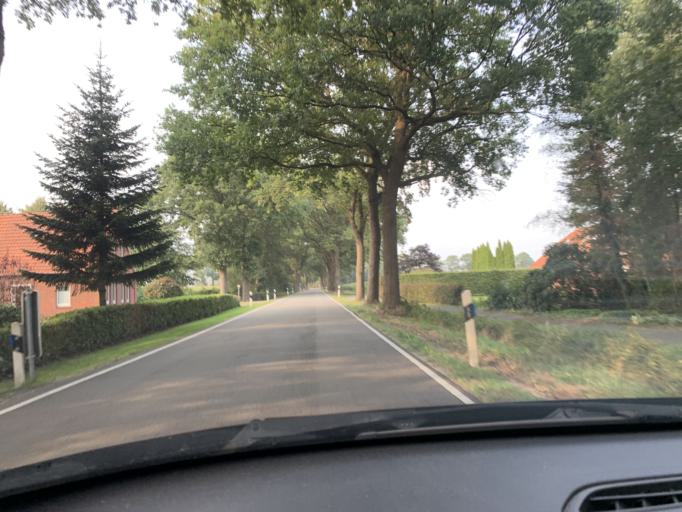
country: DE
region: Lower Saxony
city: Apen
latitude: 53.1859
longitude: 7.7823
